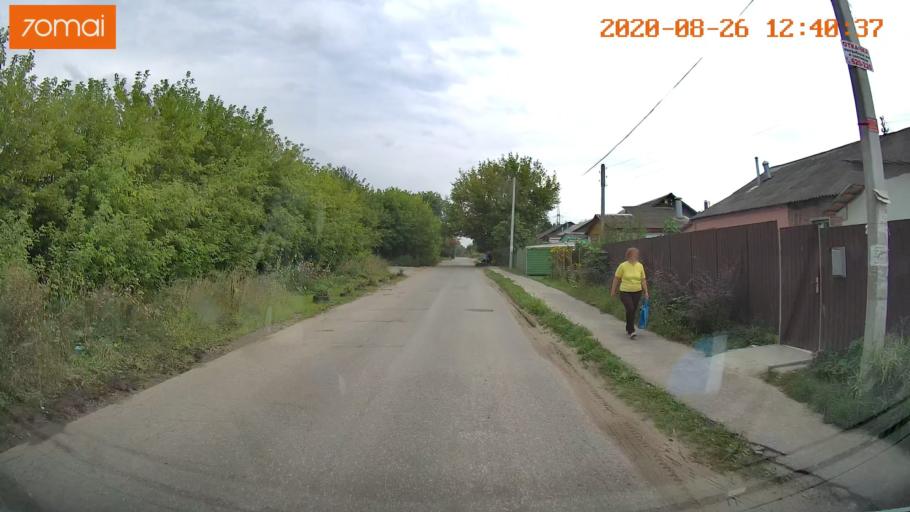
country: RU
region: Rjazan
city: Ryazan'
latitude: 54.6007
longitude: 39.7602
